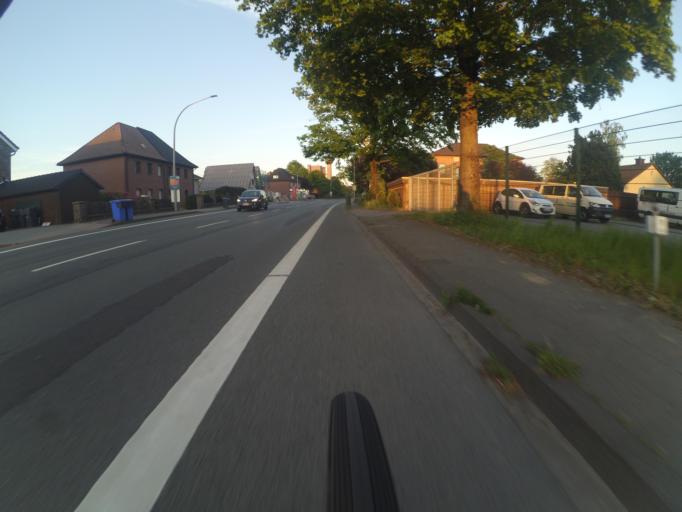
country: DE
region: North Rhine-Westphalia
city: Ibbenburen
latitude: 52.2878
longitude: 7.7301
